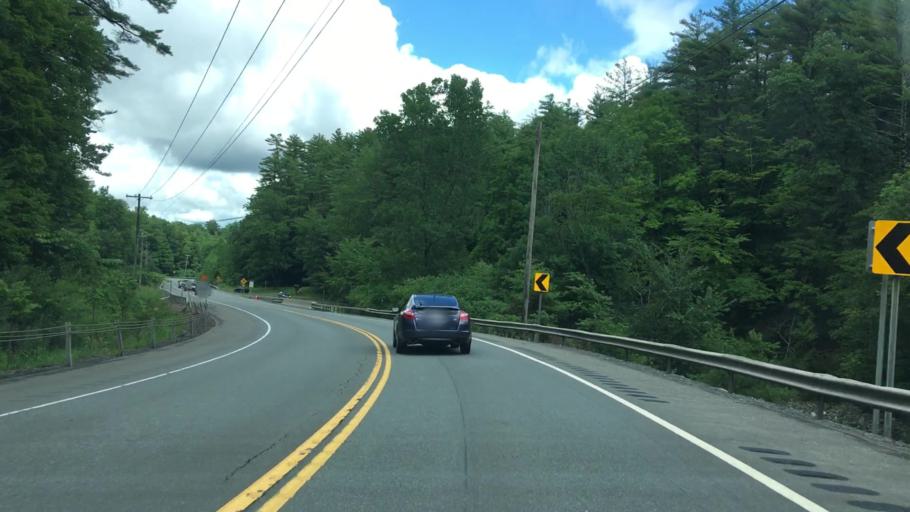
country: US
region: New York
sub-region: Rensselaer County
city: Hoosick Falls
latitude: 42.8465
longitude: -73.3506
